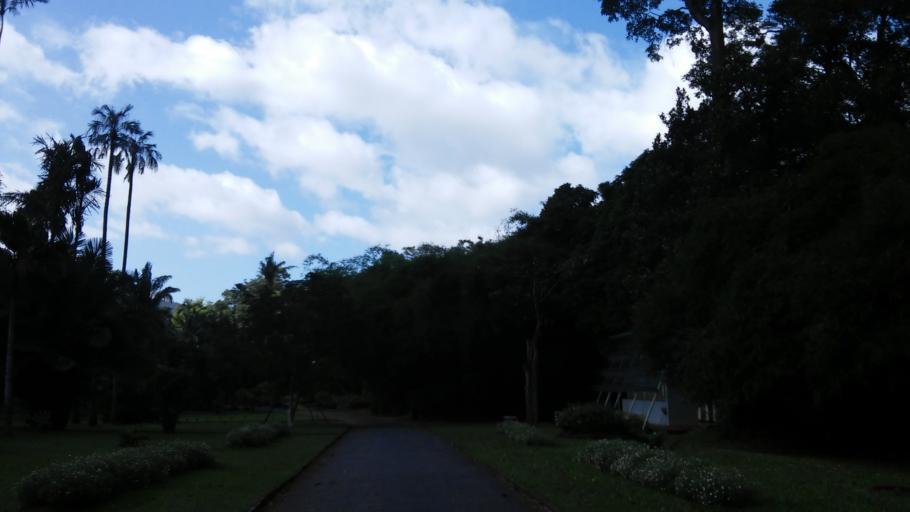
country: LK
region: Central
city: Kandy
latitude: 7.2666
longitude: 80.5941
